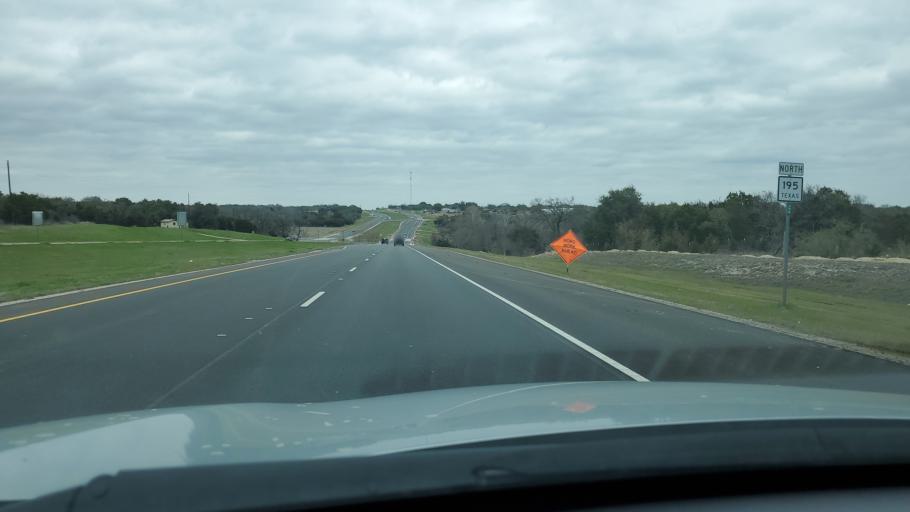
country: US
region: Texas
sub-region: Williamson County
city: Florence
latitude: 30.9207
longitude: -97.7949
